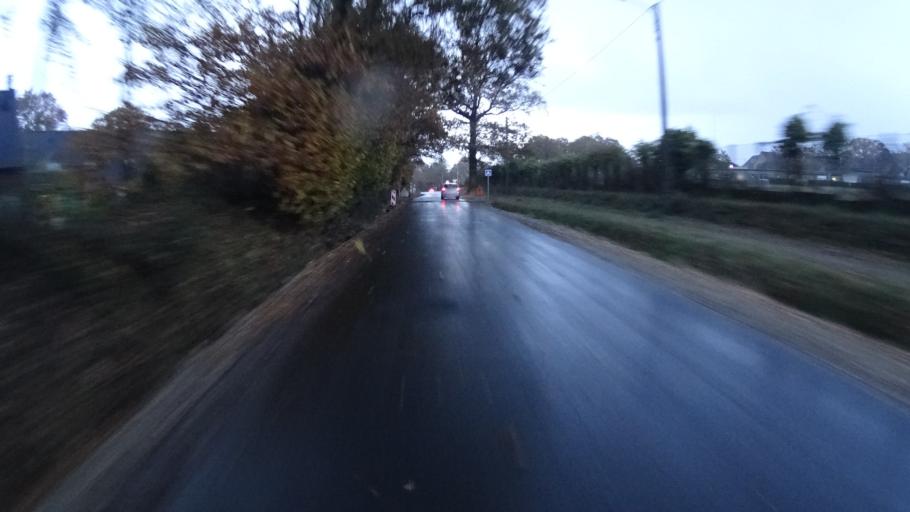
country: FR
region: Pays de la Loire
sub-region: Departement de la Loire-Atlantique
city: Saint-Nicolas-de-Redon
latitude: 47.6601
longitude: -2.0675
